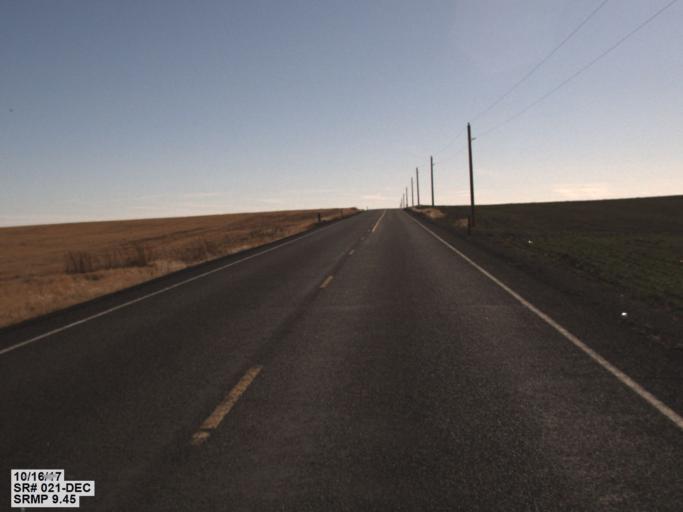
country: US
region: Washington
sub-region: Franklin County
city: Connell
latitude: 46.7630
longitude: -118.5476
